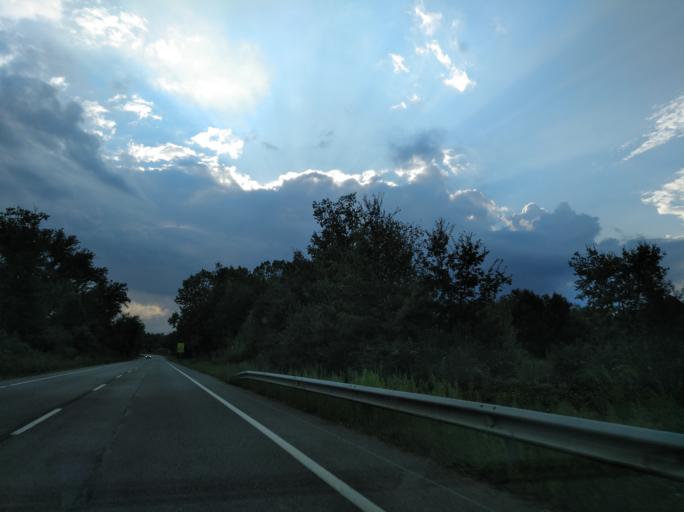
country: ES
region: Catalonia
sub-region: Provincia de Girona
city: Brunyola
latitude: 41.8895
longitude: 2.7122
